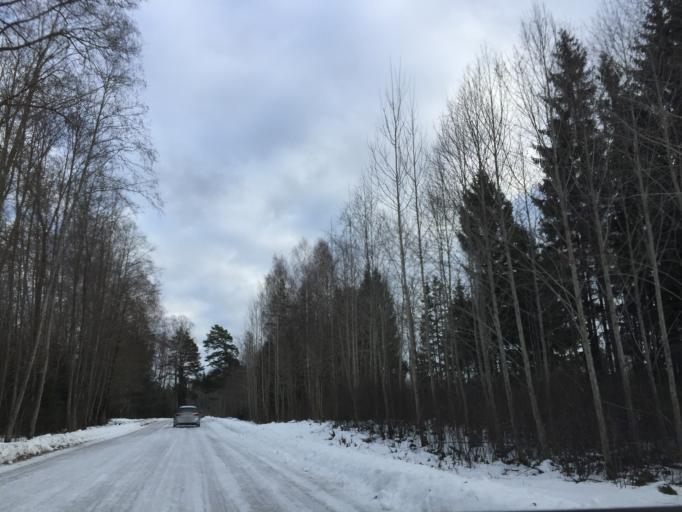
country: LV
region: Lielvarde
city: Lielvarde
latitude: 56.5806
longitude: 24.7663
